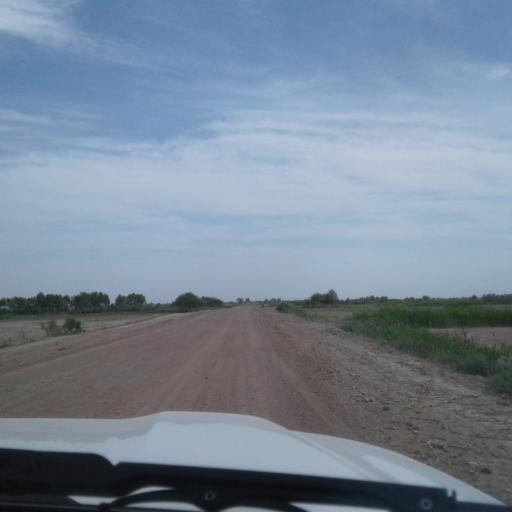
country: TM
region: Dasoguz
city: Tagta
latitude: 41.5480
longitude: 59.8114
